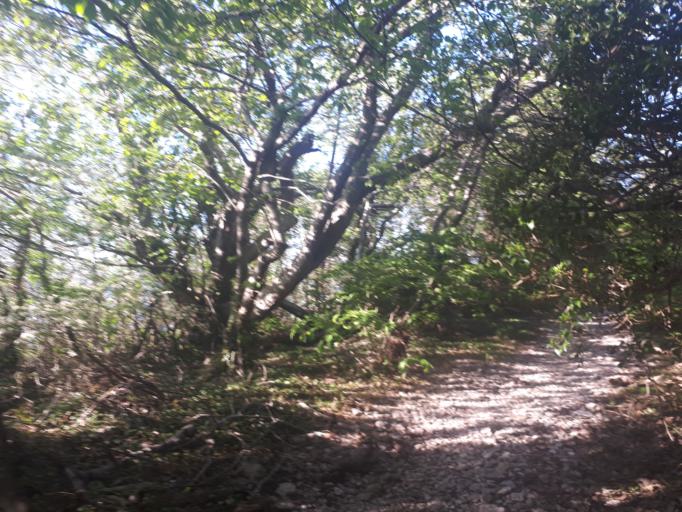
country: SE
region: Gotland
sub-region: Gotland
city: Vibble
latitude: 57.6121
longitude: 18.2468
